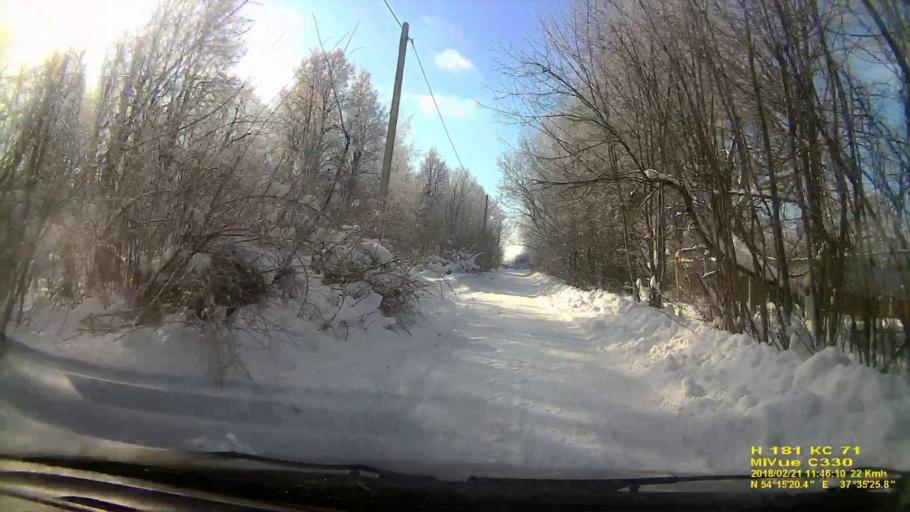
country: RU
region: Tula
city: Gorelki
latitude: 54.2556
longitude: 37.5904
